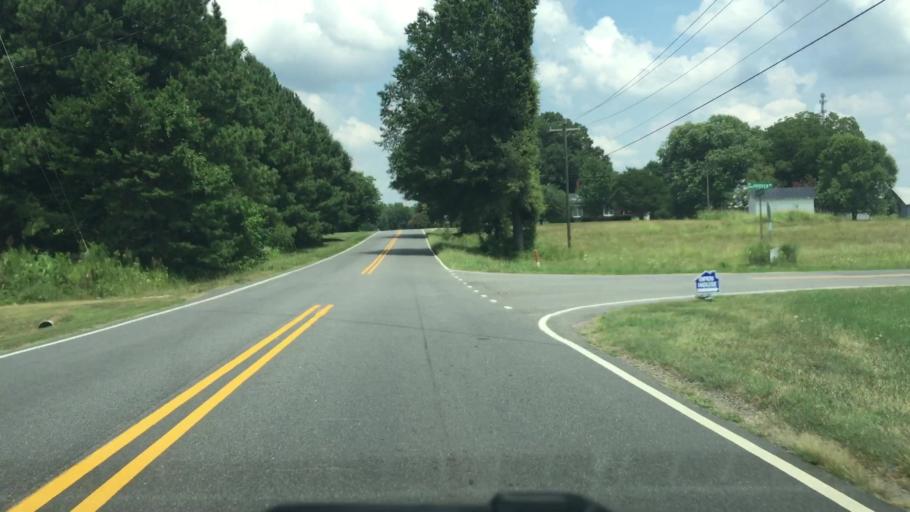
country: US
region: North Carolina
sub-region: Iredell County
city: Troutman
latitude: 35.7232
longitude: -80.8717
